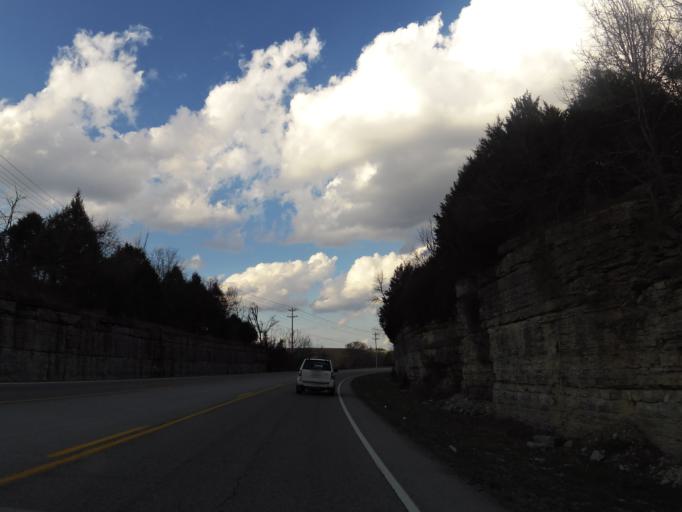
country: US
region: Tennessee
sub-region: Smith County
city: South Carthage
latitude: 36.2154
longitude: -85.9537
